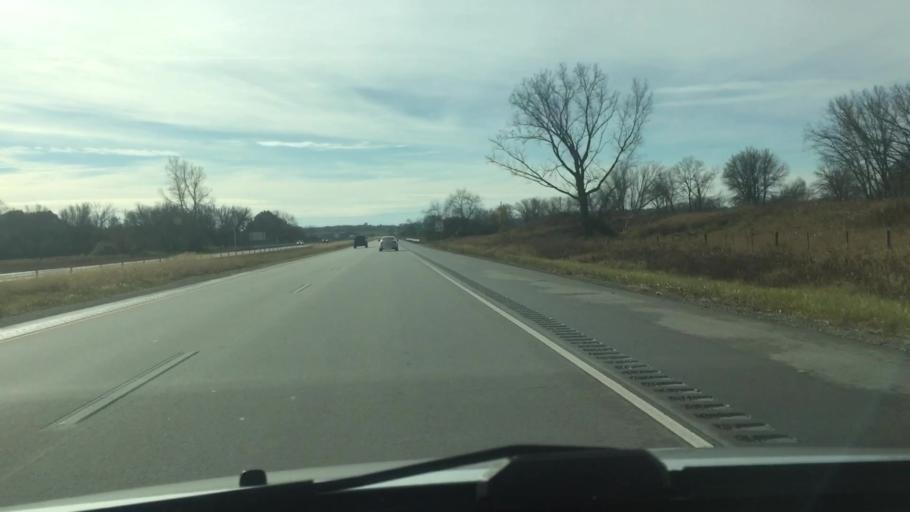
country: US
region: Wisconsin
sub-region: Waukesha County
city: Pewaukee
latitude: 43.0615
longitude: -88.2517
